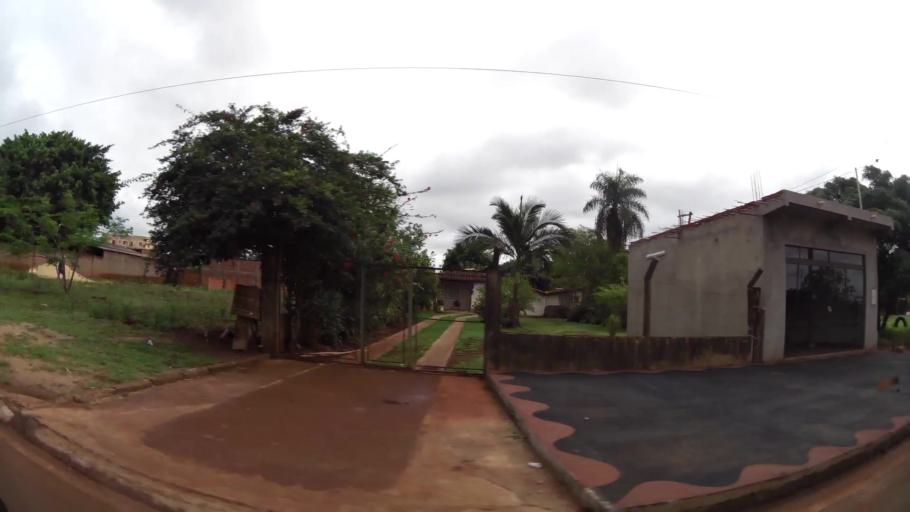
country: PY
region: Alto Parana
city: Ciudad del Este
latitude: -25.3862
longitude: -54.6441
